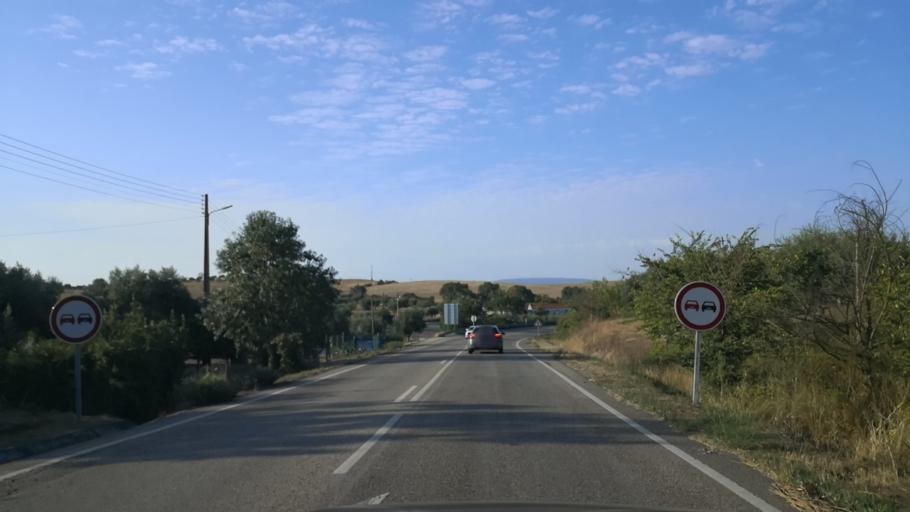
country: PT
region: Santarem
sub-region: Santarem
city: Santarem
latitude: 39.3174
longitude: -8.6702
